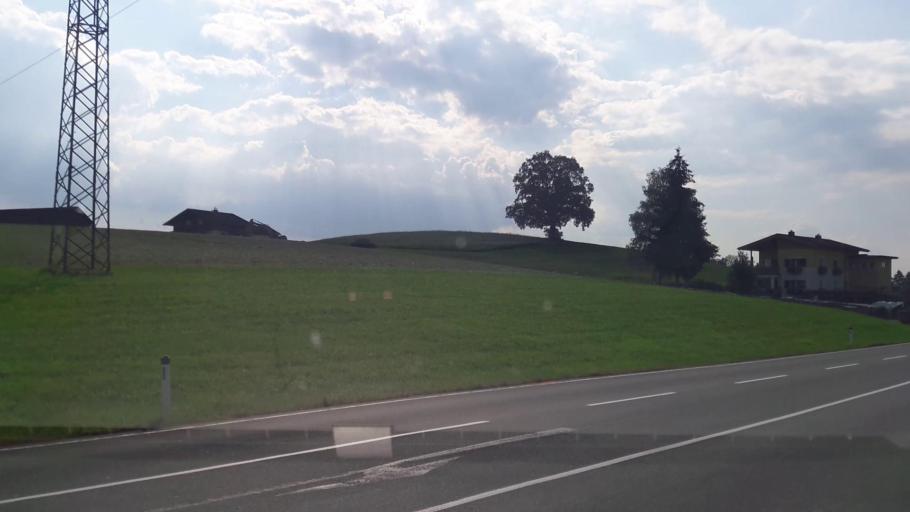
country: AT
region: Salzburg
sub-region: Politischer Bezirk Salzburg-Umgebung
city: Henndorf am Wallersee
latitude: 47.8880
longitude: 13.1876
